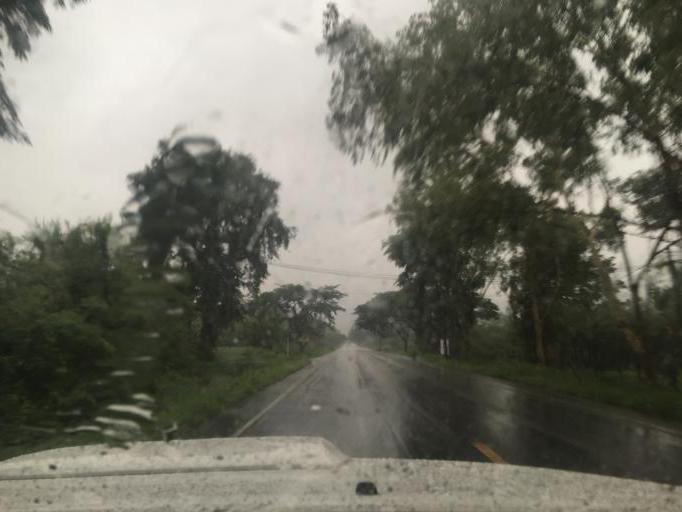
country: TH
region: Changwat Udon Thani
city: Udon Thani
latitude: 17.3507
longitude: 102.7193
